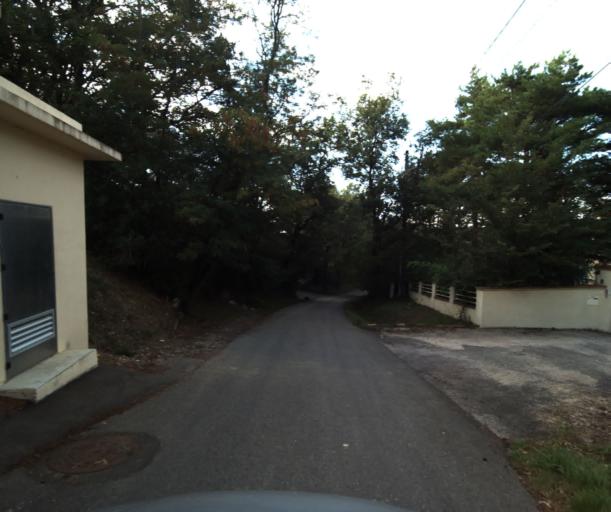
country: FR
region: Midi-Pyrenees
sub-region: Departement de la Haute-Garonne
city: Saubens
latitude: 43.4752
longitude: 1.3488
